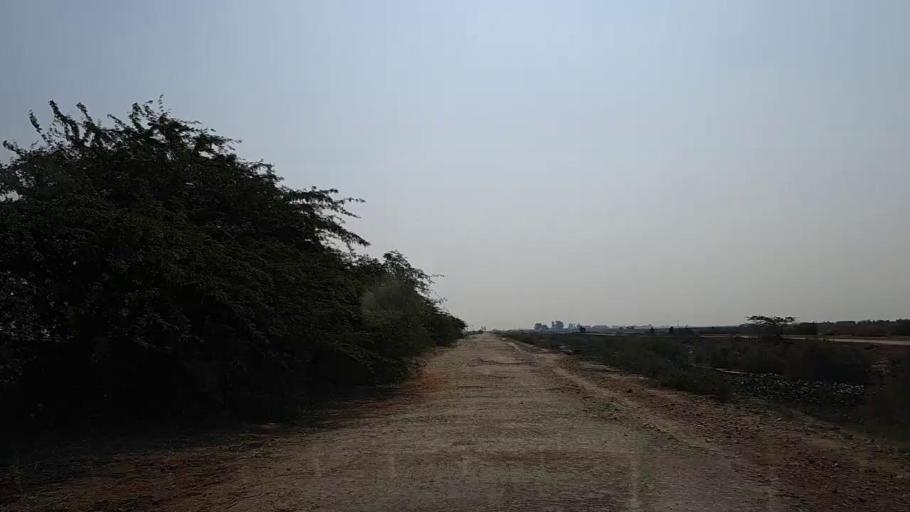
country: PK
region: Sindh
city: Thatta
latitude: 24.7186
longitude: 67.7684
